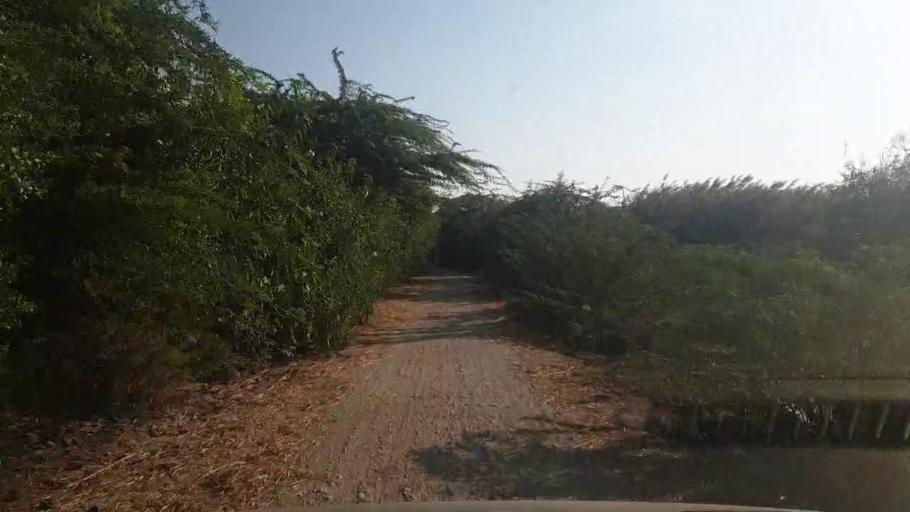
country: PK
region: Sindh
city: Tando Bago
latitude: 24.7456
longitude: 68.9308
